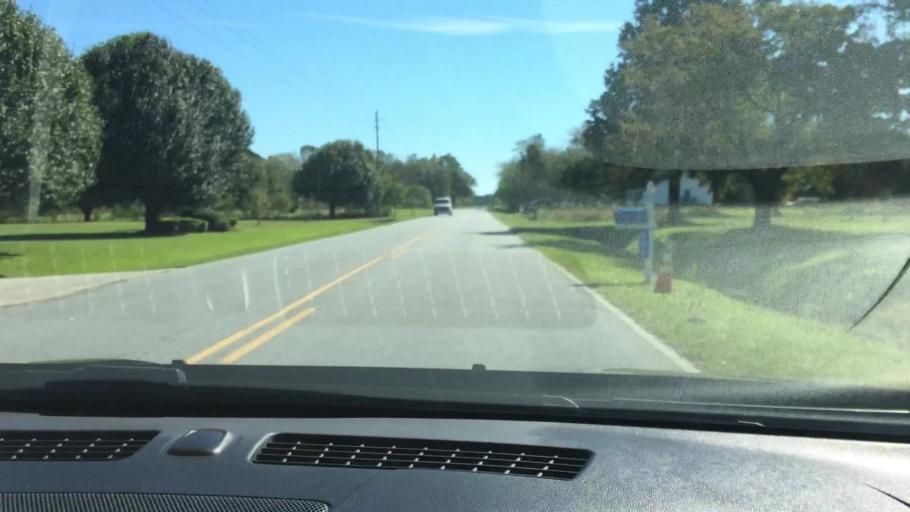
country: US
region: North Carolina
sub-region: Pitt County
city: Grifton
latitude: 35.4051
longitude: -77.4208
